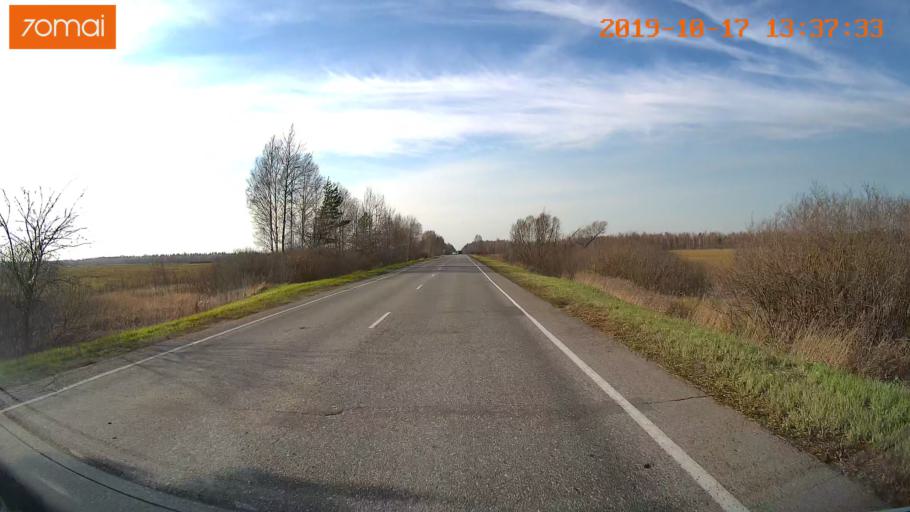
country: RU
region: Rjazan
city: Tuma
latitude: 55.1419
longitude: 40.6361
